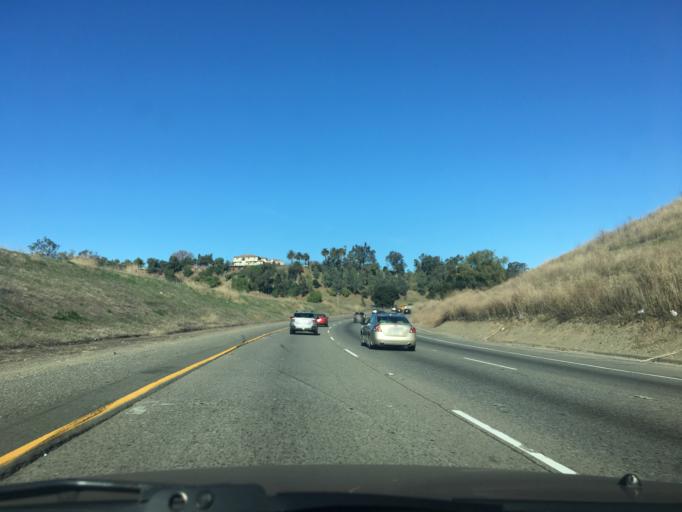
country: US
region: California
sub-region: Alameda County
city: Fremont
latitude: 37.5254
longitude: -121.9461
